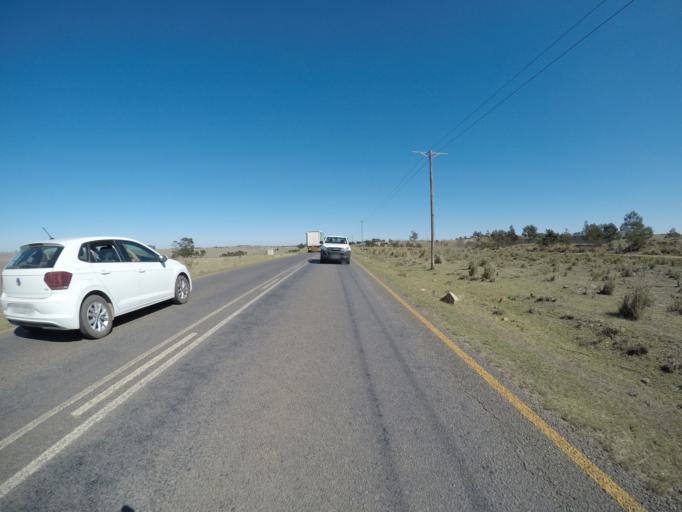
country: ZA
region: Eastern Cape
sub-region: OR Tambo District Municipality
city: Mthatha
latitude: -31.8024
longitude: 28.7512
